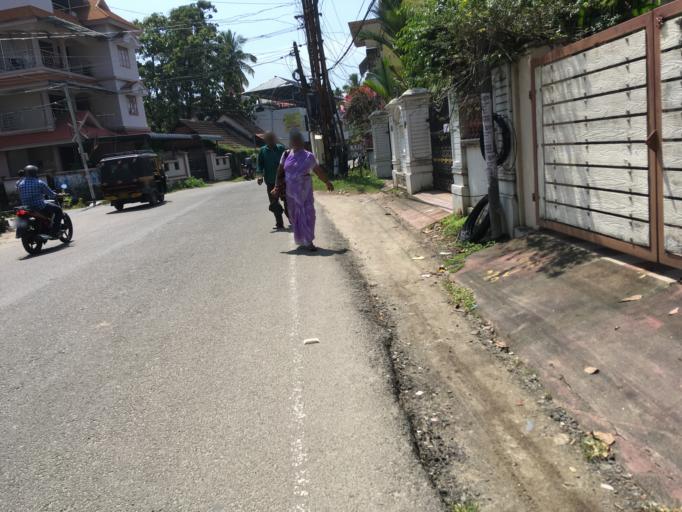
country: IN
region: Kerala
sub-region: Ernakulam
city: Cochin
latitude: 9.9612
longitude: 76.2458
